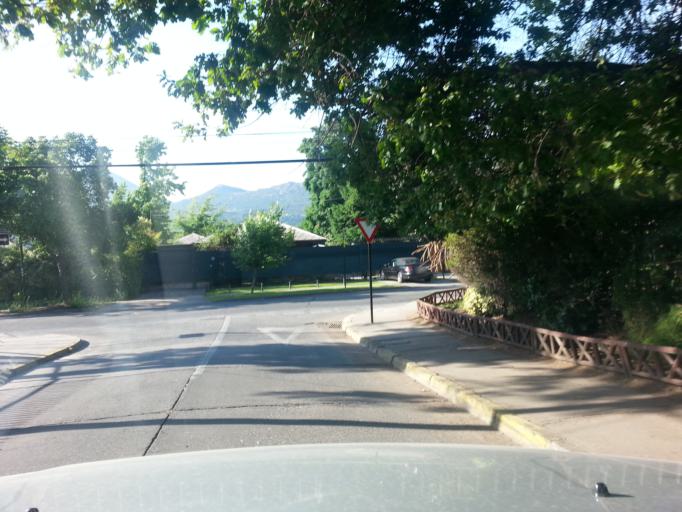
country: CL
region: Santiago Metropolitan
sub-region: Provincia de Santiago
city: Villa Presidente Frei, Nunoa, Santiago, Chile
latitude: -33.3856
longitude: -70.5478
